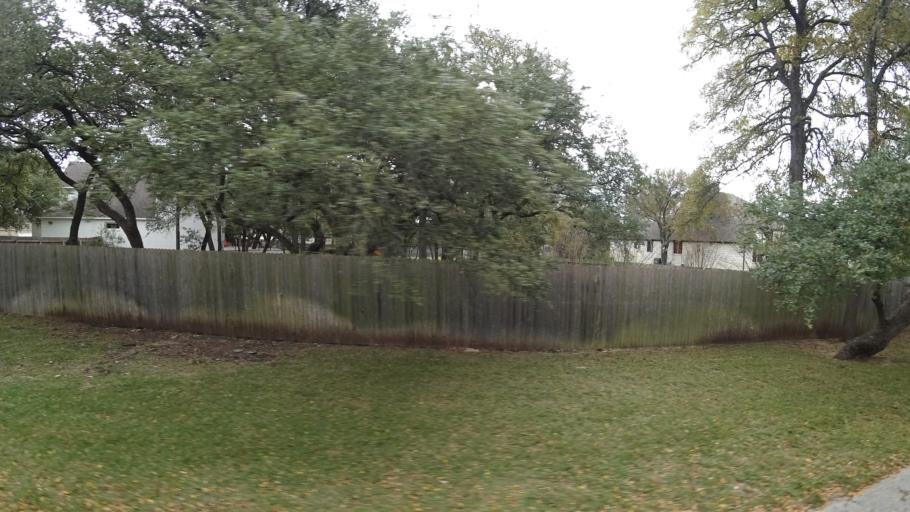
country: US
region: Texas
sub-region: Travis County
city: Barton Creek
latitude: 30.2563
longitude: -97.9084
